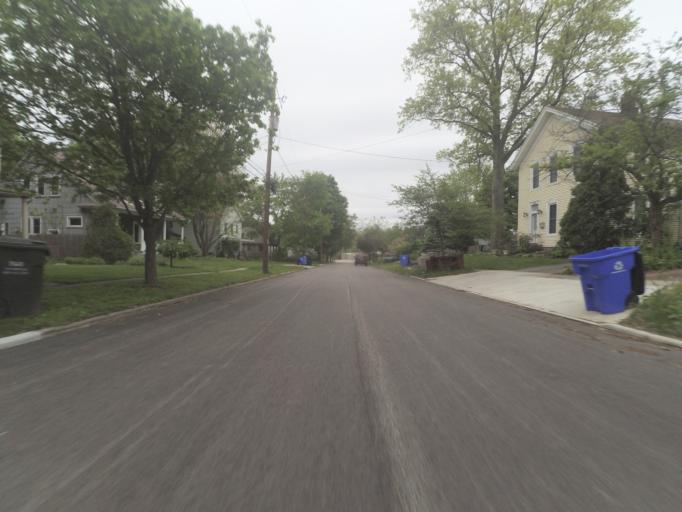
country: US
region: Ohio
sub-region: Portage County
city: Kent
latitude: 41.1581
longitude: -81.3621
